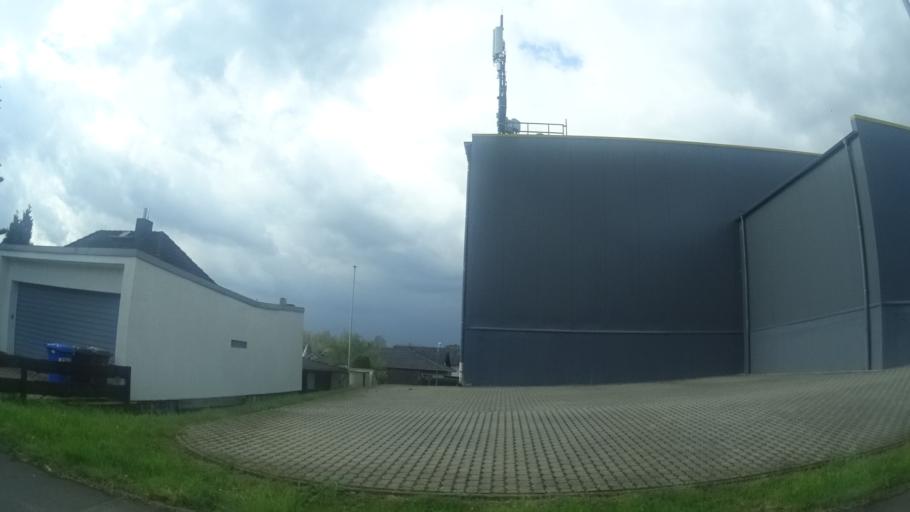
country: DE
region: Hesse
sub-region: Regierungsbezirk Giessen
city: Wetzlar
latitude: 50.5676
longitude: 8.5313
